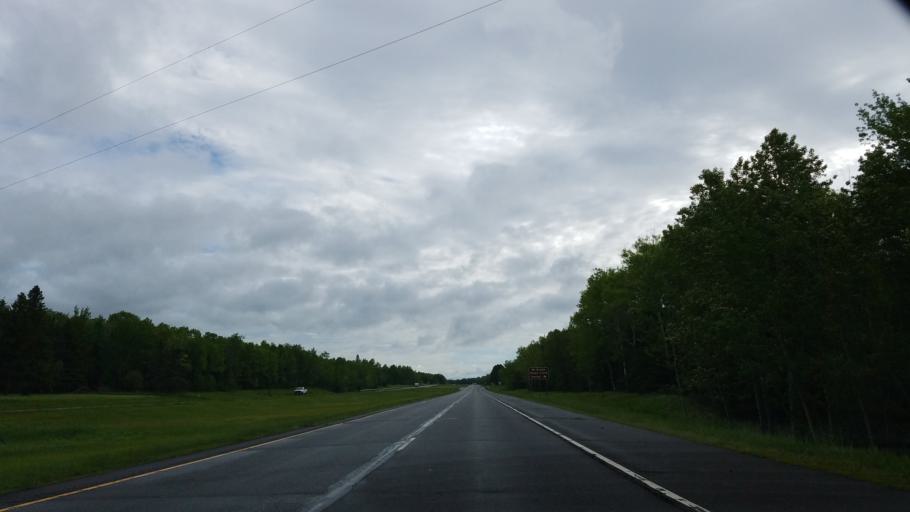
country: US
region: Minnesota
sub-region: Saint Louis County
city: Arnold
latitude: 46.8865
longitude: -91.9269
